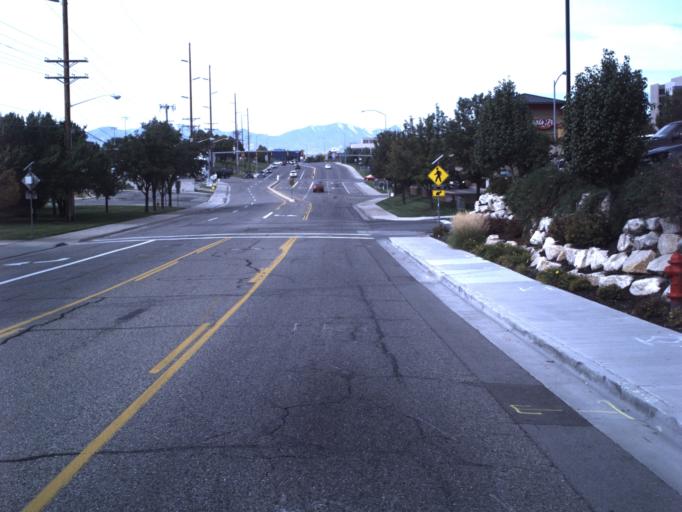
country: US
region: Utah
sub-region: Salt Lake County
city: Murray
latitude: 40.6561
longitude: -111.8856
